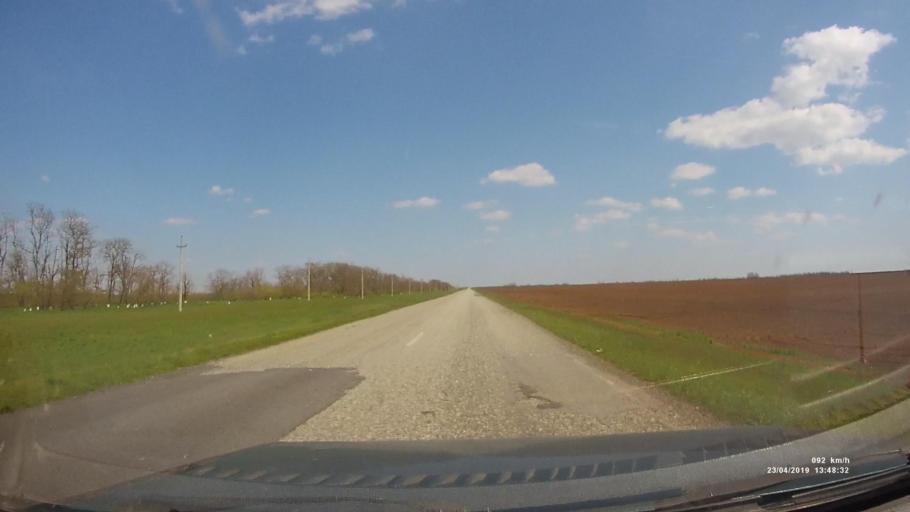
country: RU
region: Kalmykiya
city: Yashalta
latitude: 46.5992
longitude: 42.8754
